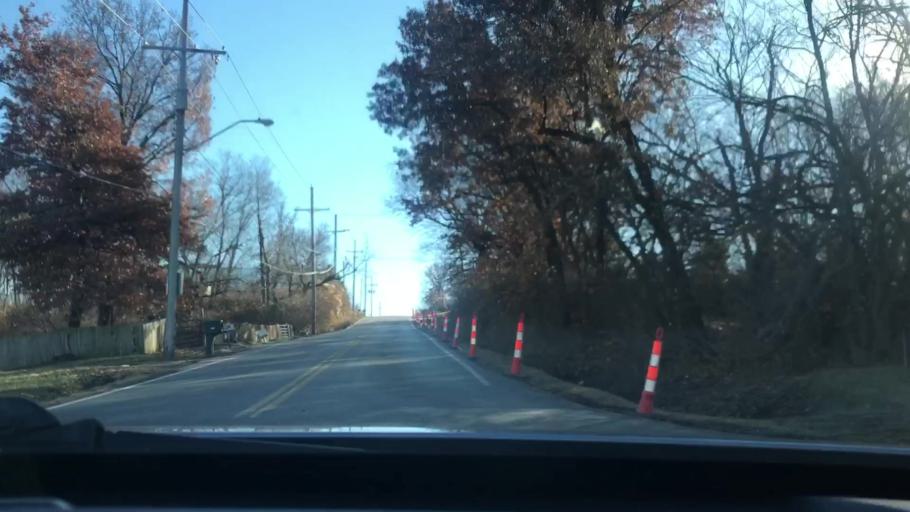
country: US
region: Missouri
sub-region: Jackson County
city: Raytown
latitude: 38.9721
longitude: -94.5209
